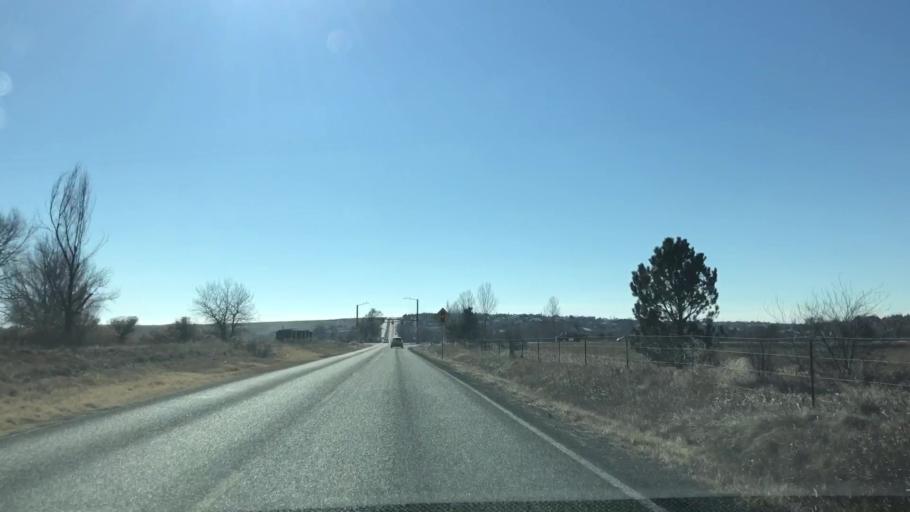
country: US
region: Colorado
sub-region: Weld County
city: Windsor
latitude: 40.4814
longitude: -104.9442
